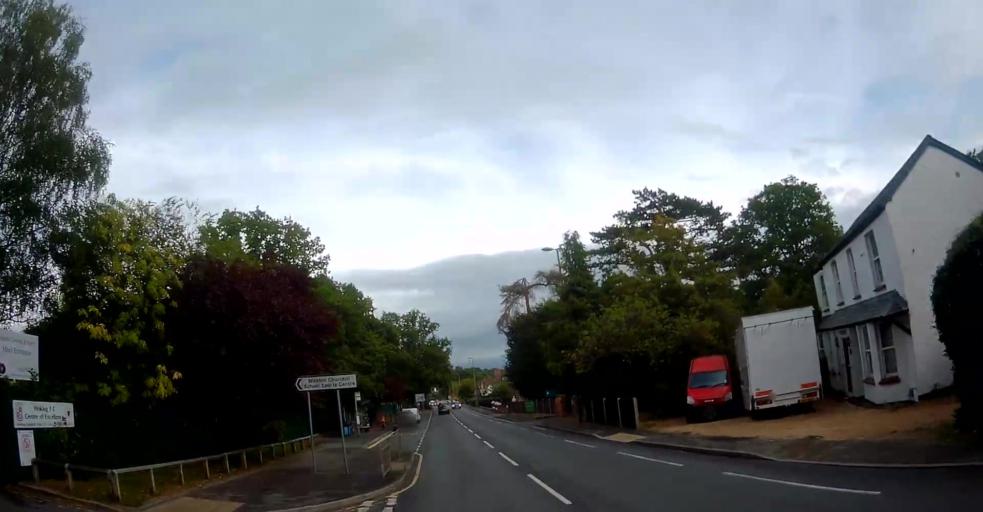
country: GB
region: England
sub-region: Surrey
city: Knaphill
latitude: 51.3125
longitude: -0.6032
